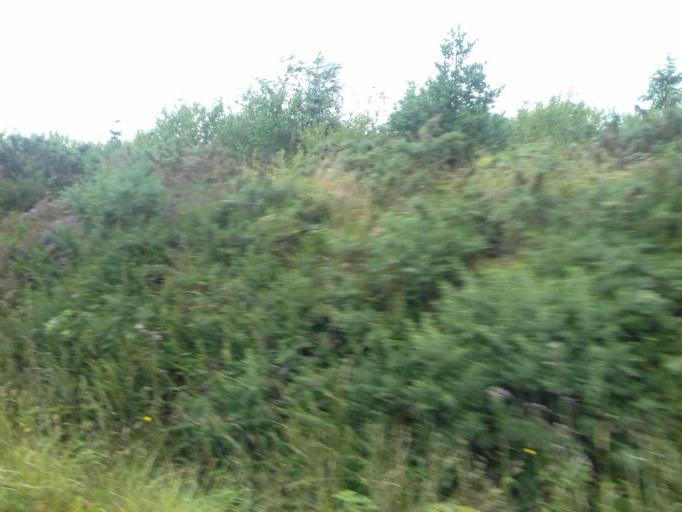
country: IE
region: Leinster
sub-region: Loch Garman
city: Bunclody
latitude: 52.6557
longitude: -6.7669
